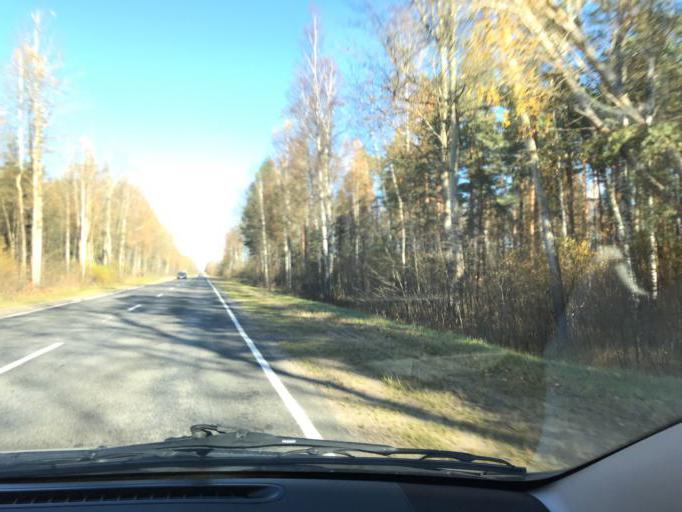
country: BY
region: Vitebsk
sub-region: Ushatski Rayon
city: Ushachy
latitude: 55.0695
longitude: 28.7538
